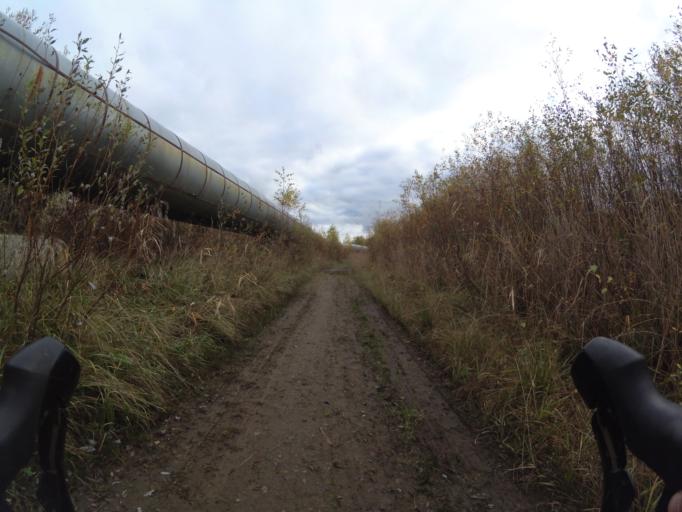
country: RU
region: St.-Petersburg
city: Lakhtinskiy
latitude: 60.0034
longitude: 30.1510
